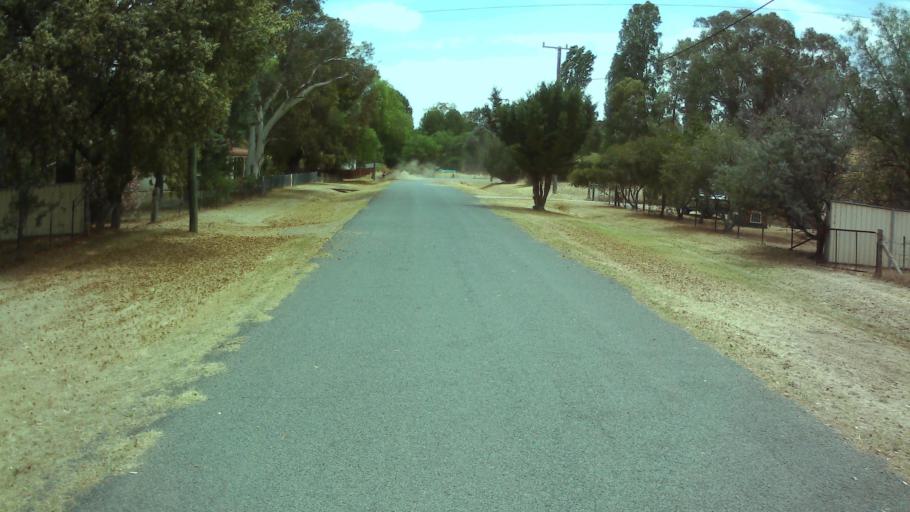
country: AU
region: New South Wales
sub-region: Weddin
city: Grenfell
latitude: -33.9956
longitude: 148.4014
